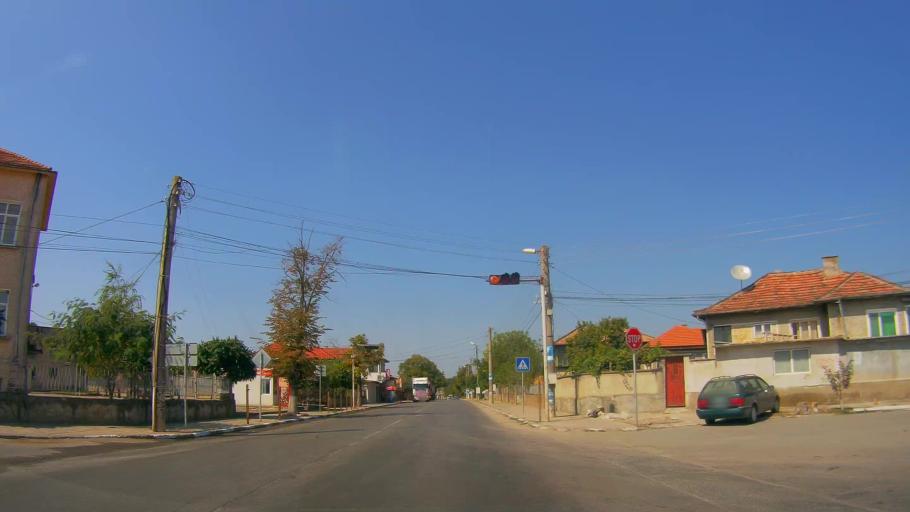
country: BG
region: Razgrad
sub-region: Obshtina Tsar Kaloyan
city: Tsar Kaloyan
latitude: 43.6060
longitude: 26.2402
